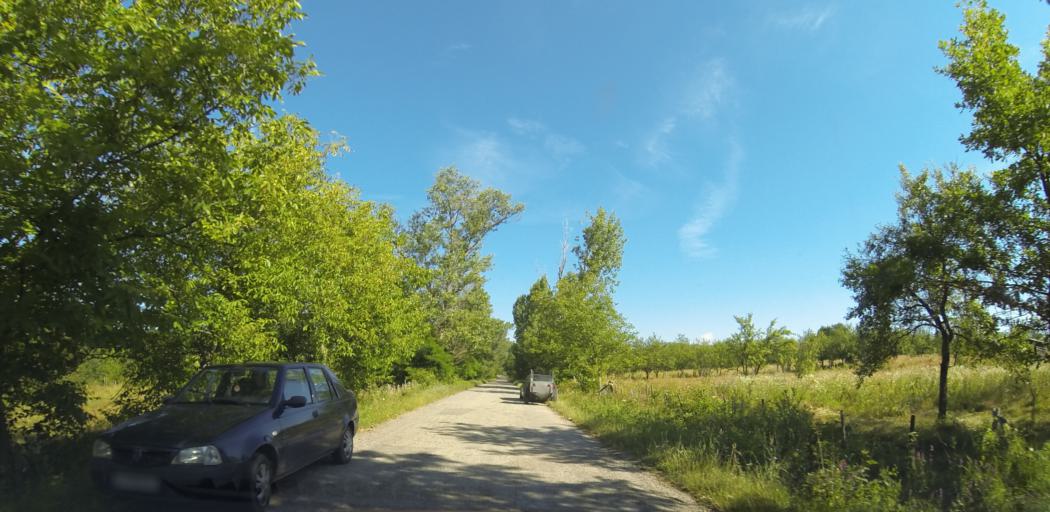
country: RO
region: Gorj
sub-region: Comuna Polovragi
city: Polovragi
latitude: 45.1684
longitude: 23.8584
